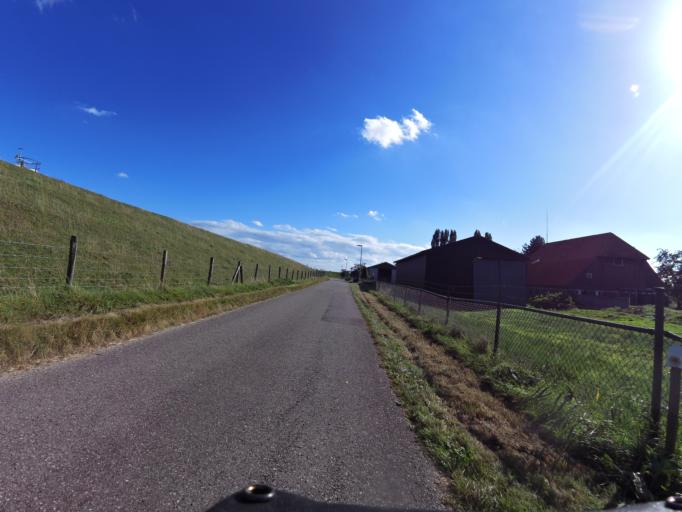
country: NL
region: South Holland
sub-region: Gemeente Zwijndrecht
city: Zwijndrecht
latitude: 51.7591
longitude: 4.6232
